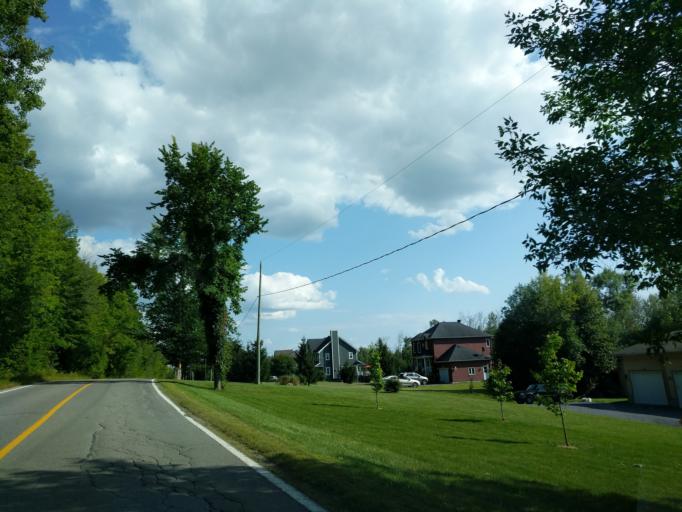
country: CA
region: Quebec
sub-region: Outaouais
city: Gatineau
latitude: 45.4727
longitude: -75.8541
